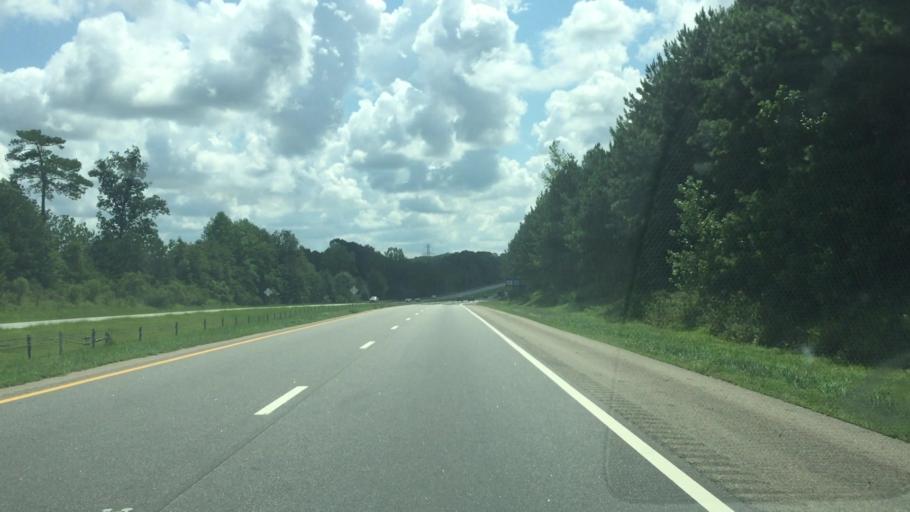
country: US
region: North Carolina
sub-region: Richmond County
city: Cordova
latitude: 34.9192
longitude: -79.8068
